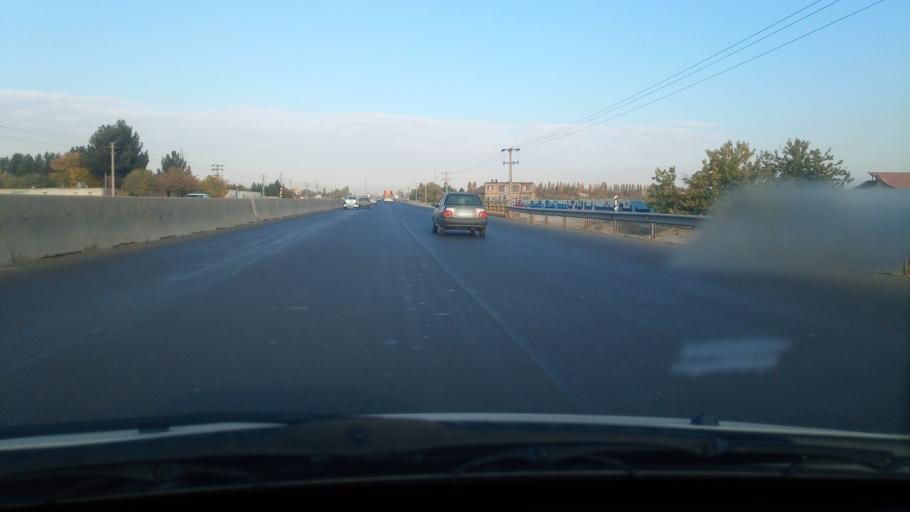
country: IR
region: Razavi Khorasan
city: Chenaran
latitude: 36.5457
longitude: 59.2693
